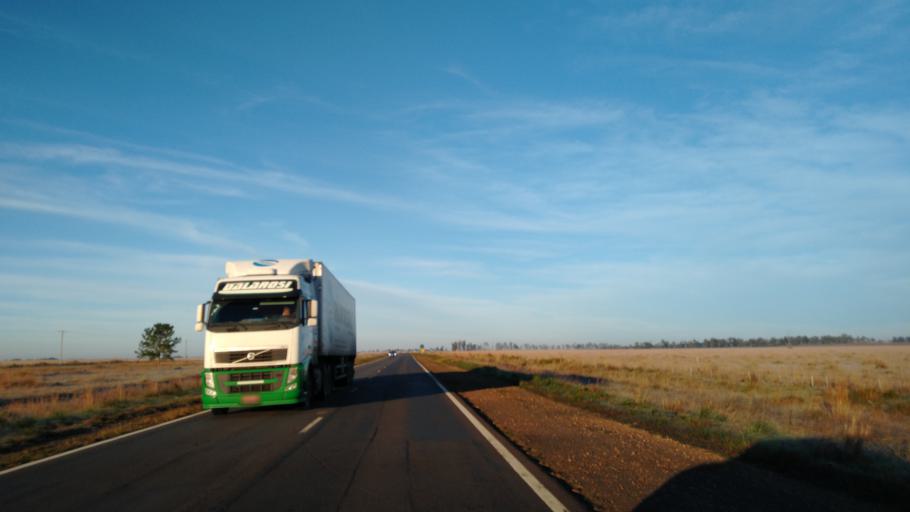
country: AR
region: Corrientes
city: Santo Tome
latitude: -28.6174
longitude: -56.1103
